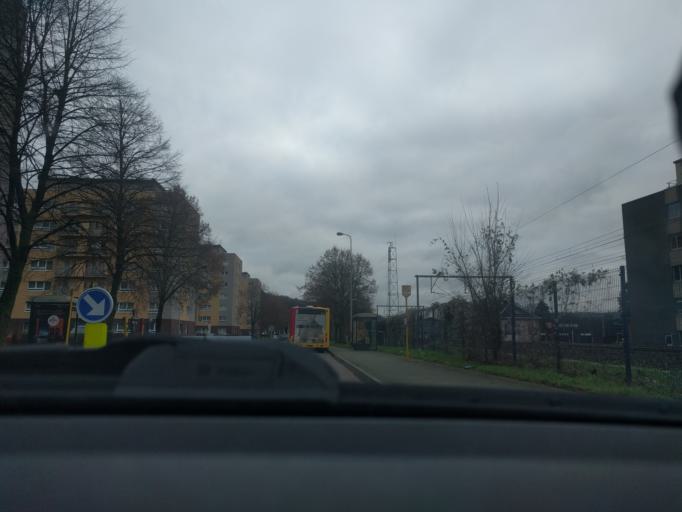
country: BE
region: Wallonia
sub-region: Province de Namur
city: Namur
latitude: 50.4687
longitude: 4.8875
